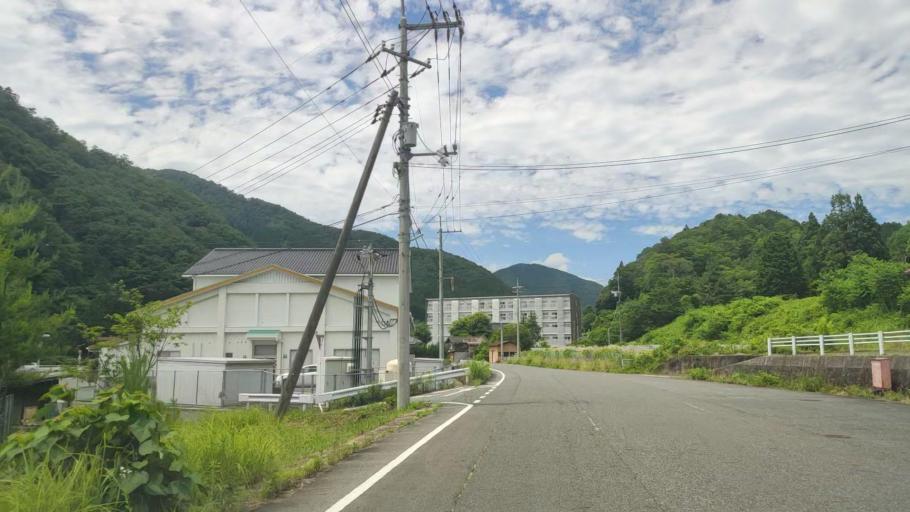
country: JP
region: Hyogo
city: Yamazakicho-nakabirose
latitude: 35.1083
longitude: 134.3281
